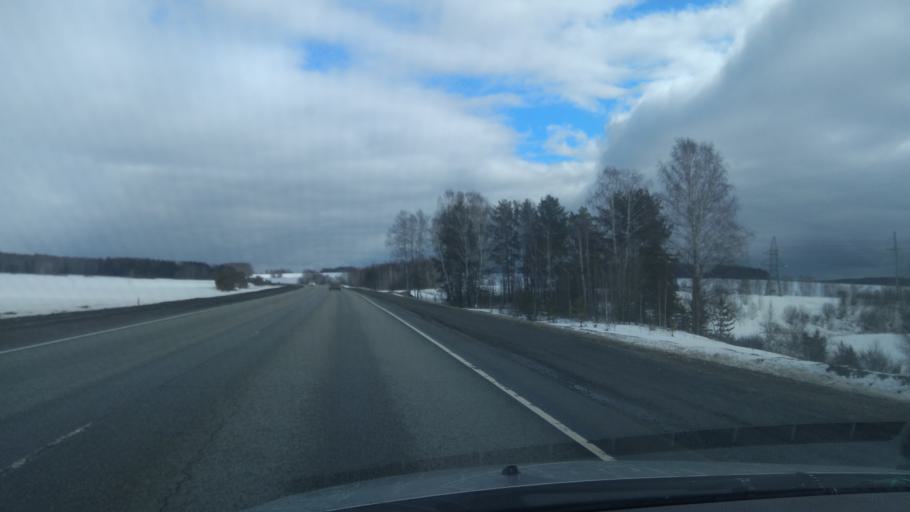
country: RU
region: Sverdlovsk
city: Ufimskiy
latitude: 56.7726
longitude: 58.0160
